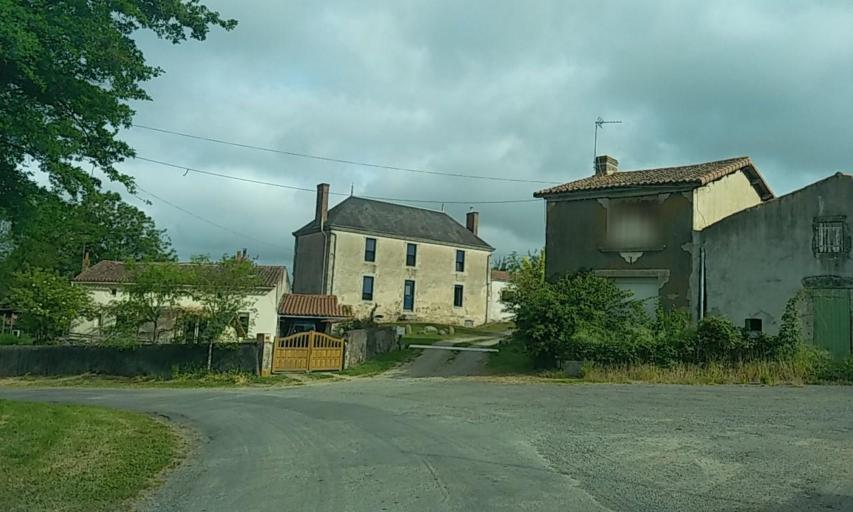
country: FR
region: Poitou-Charentes
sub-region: Departement des Deux-Sevres
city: Boisme
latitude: 46.7671
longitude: -0.4250
